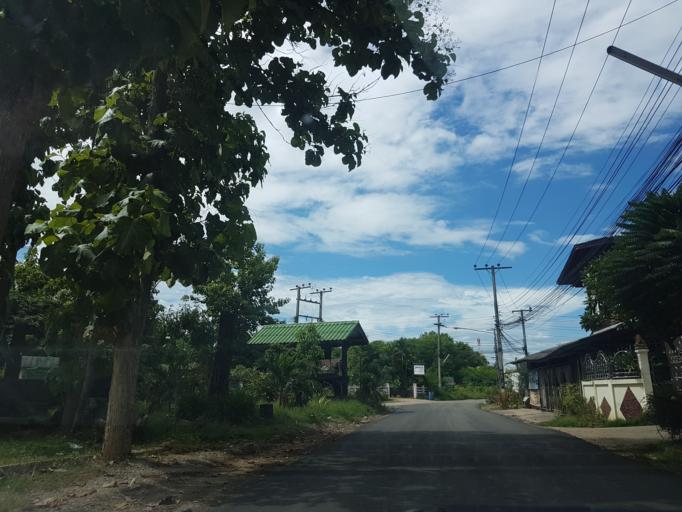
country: TH
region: Lampang
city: Ko Kha
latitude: 18.2390
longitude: 99.4323
